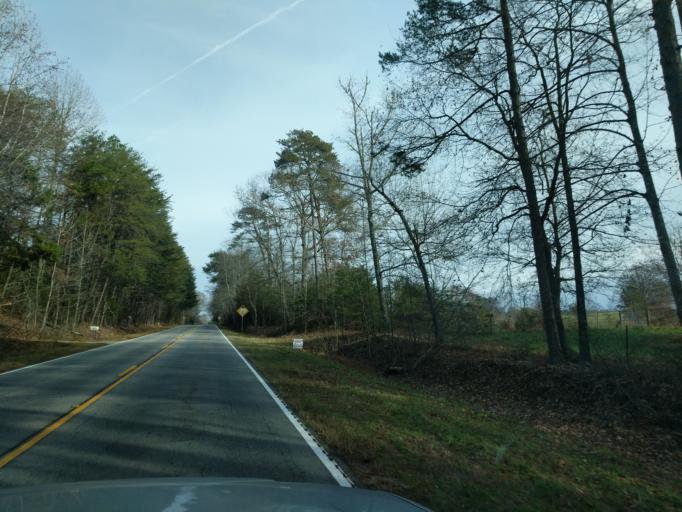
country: US
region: South Carolina
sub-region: Pickens County
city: Liberty
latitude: 34.7049
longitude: -82.6345
